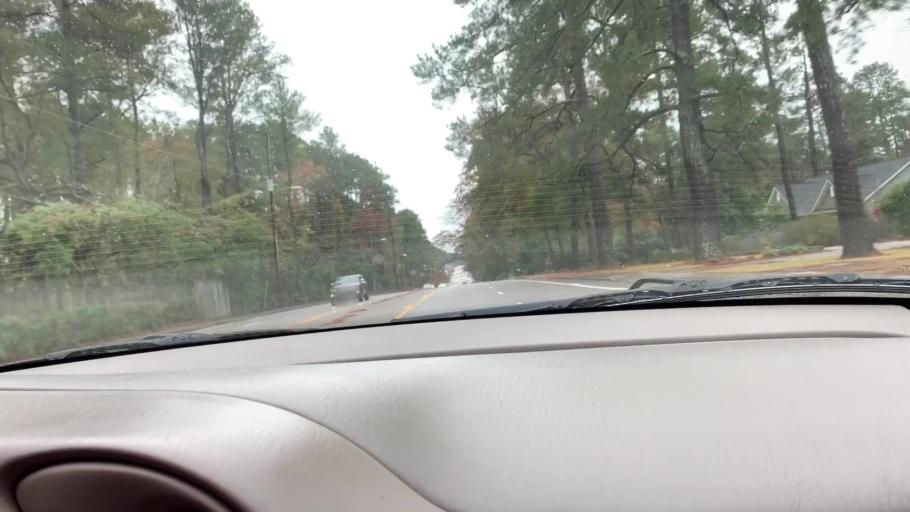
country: US
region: South Carolina
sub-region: Richland County
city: Forest Acres
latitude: 34.0271
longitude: -80.9664
